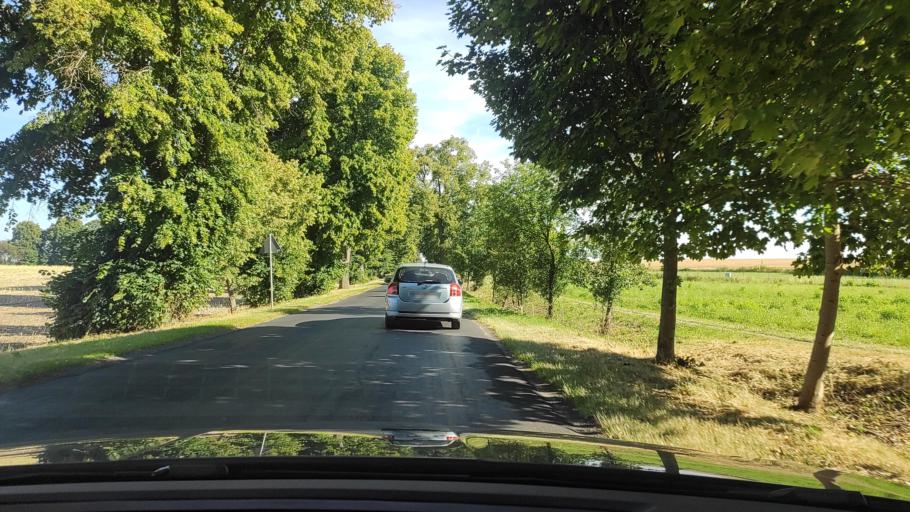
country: PL
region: Greater Poland Voivodeship
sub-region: Powiat poznanski
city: Kobylnica
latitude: 52.4869
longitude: 17.0924
